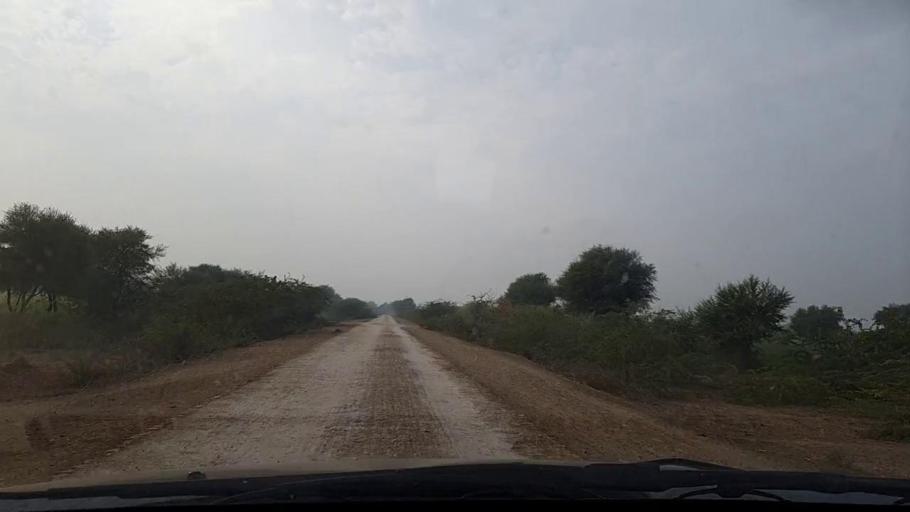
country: PK
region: Sindh
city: Pithoro
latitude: 25.7100
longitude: 69.3932
